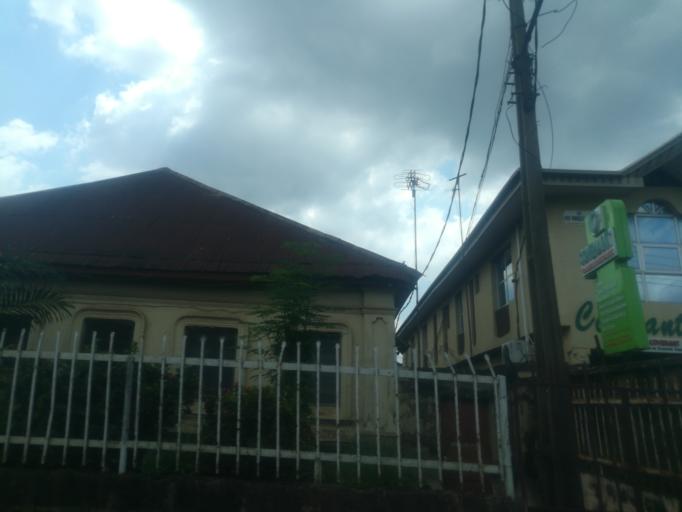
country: NG
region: Oyo
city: Ibadan
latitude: 7.3899
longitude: 3.8837
